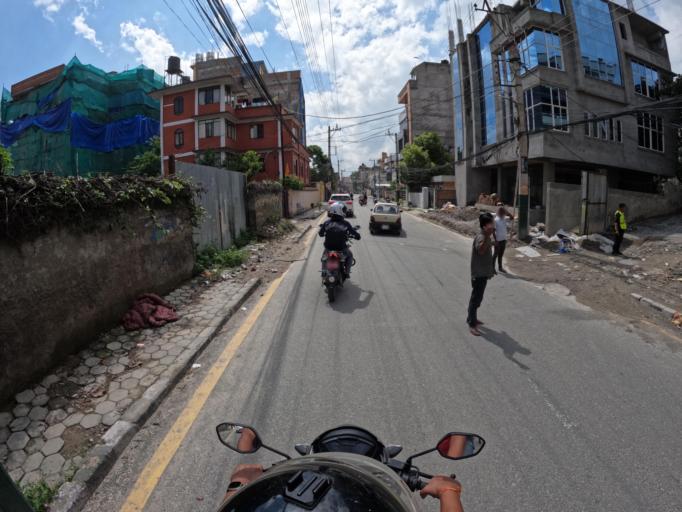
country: NP
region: Central Region
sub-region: Bagmati Zone
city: Patan
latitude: 27.6873
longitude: 85.3112
